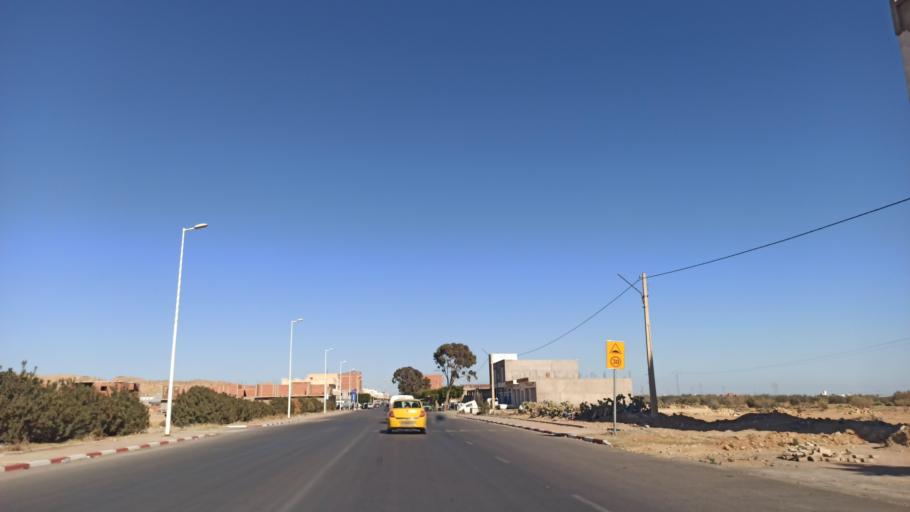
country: TN
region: Sidi Bu Zayd
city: Bi'r al Hufayy
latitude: 34.9179
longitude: 9.1859
